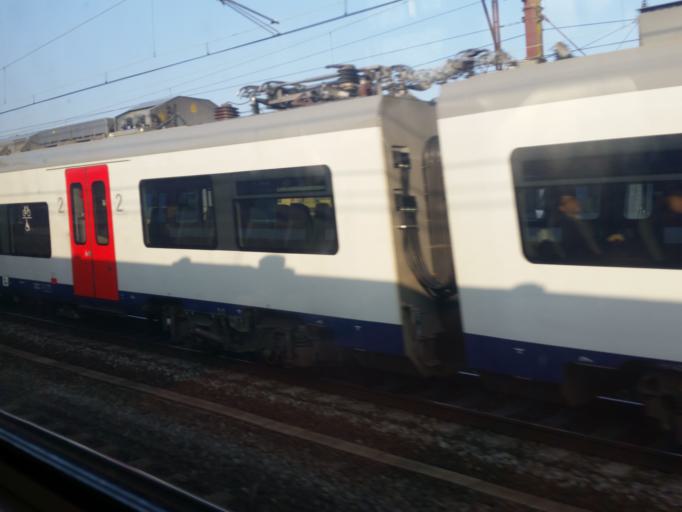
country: BE
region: Brussels Capital
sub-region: Bruxelles-Capitale
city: Brussels
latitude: 50.8726
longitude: 4.3694
